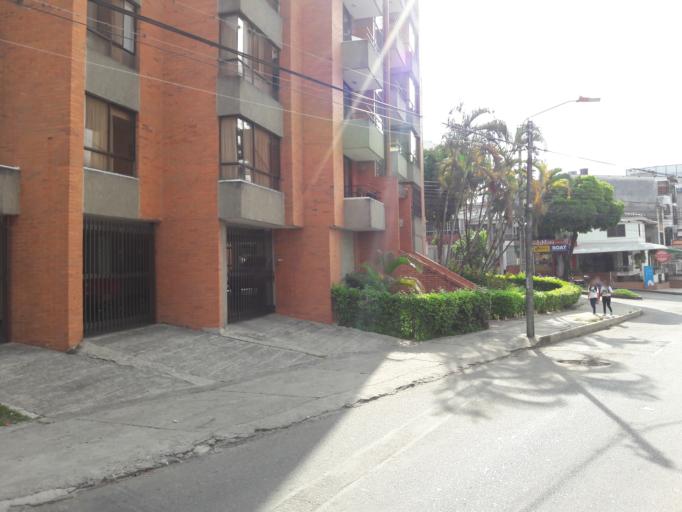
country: CO
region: Tolima
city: Ibague
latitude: 4.4360
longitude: -75.2088
